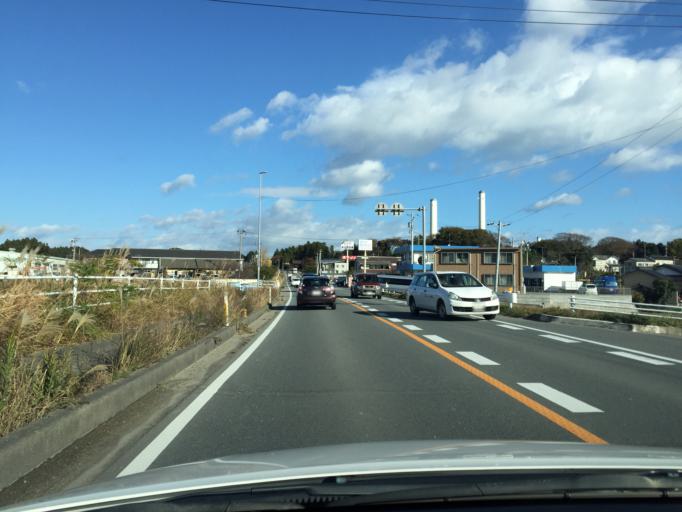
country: JP
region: Fukushima
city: Iwaki
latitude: 37.2198
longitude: 141.0017
